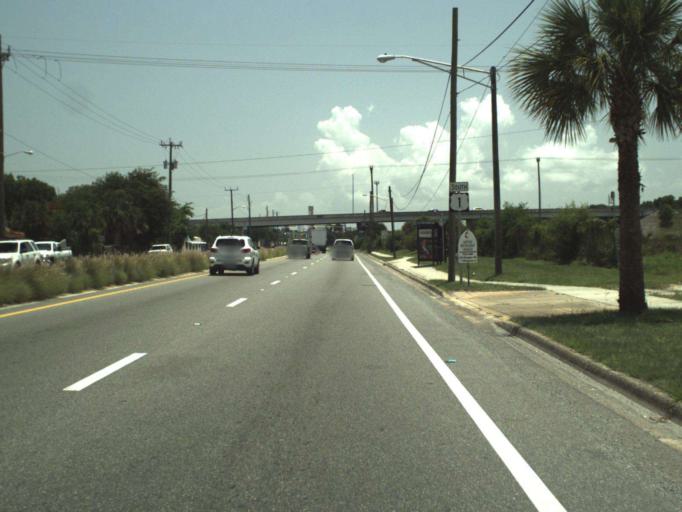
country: US
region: Florida
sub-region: Volusia County
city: New Smyrna Beach
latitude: 29.0233
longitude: -80.9264
